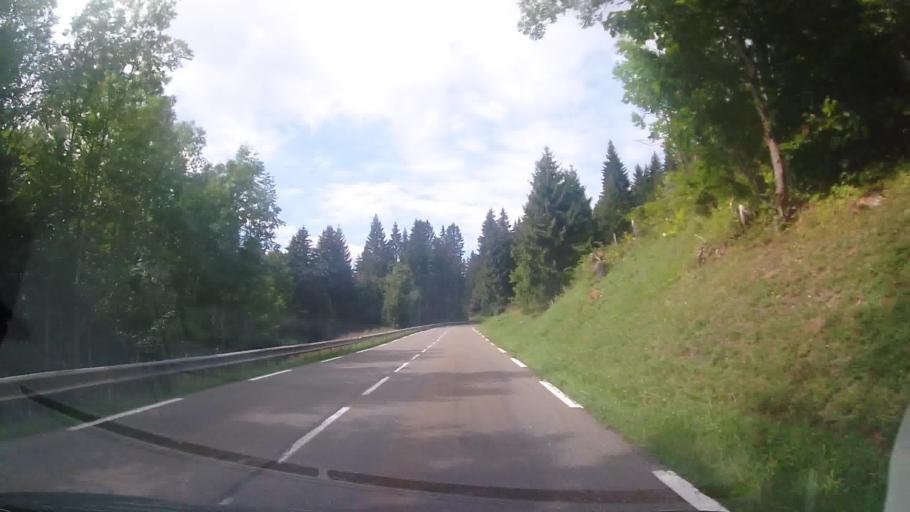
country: FR
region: Franche-Comte
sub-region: Departement du Jura
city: Les Rousses
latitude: 46.4115
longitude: 6.0637
